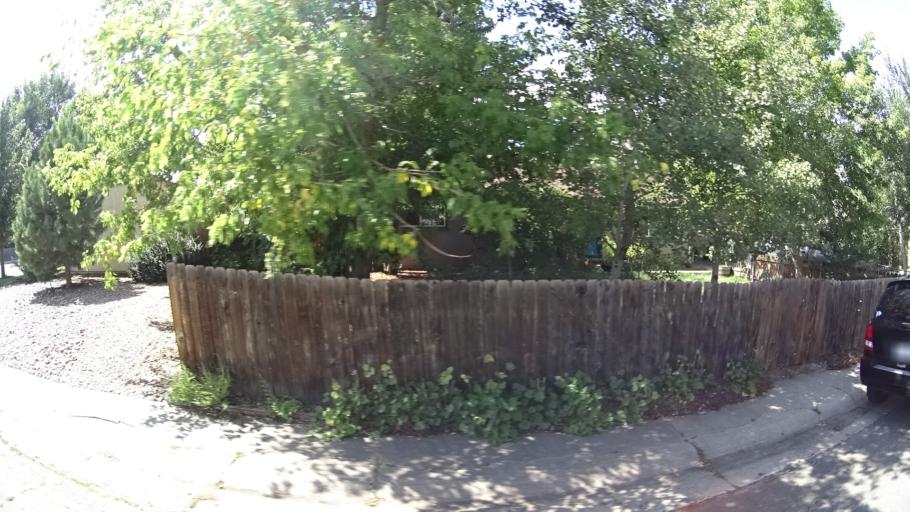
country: US
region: Colorado
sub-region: El Paso County
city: Colorado Springs
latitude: 38.8769
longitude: -104.8087
